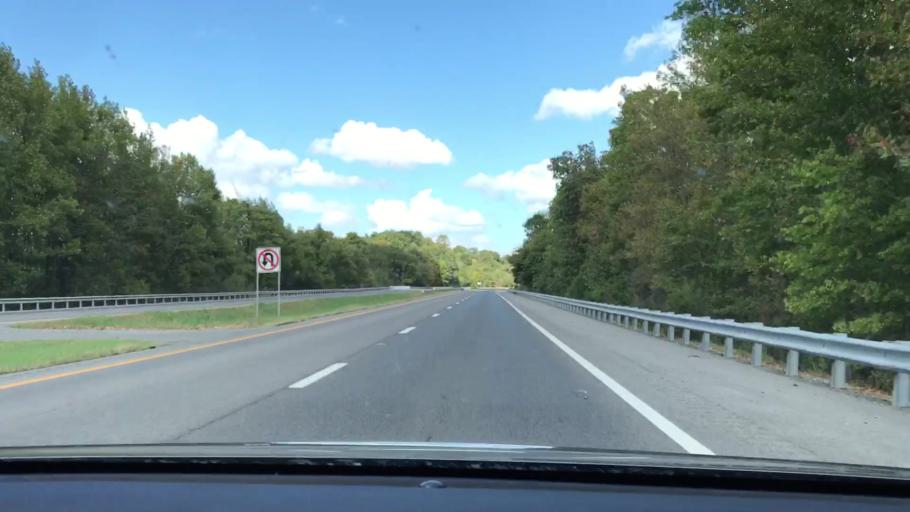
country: US
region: Kentucky
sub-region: Marshall County
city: Benton
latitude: 36.8134
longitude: -88.4880
